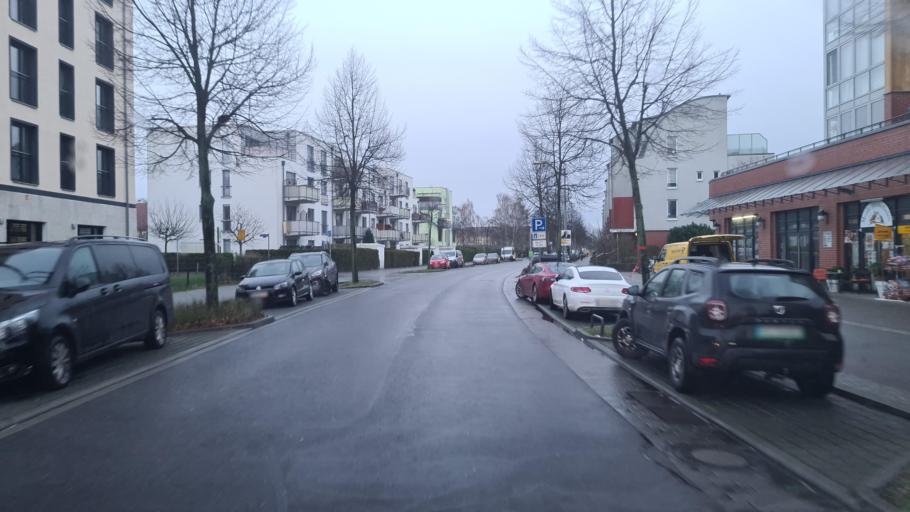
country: DE
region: Brandenburg
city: Teltow
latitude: 52.3932
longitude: 13.2713
